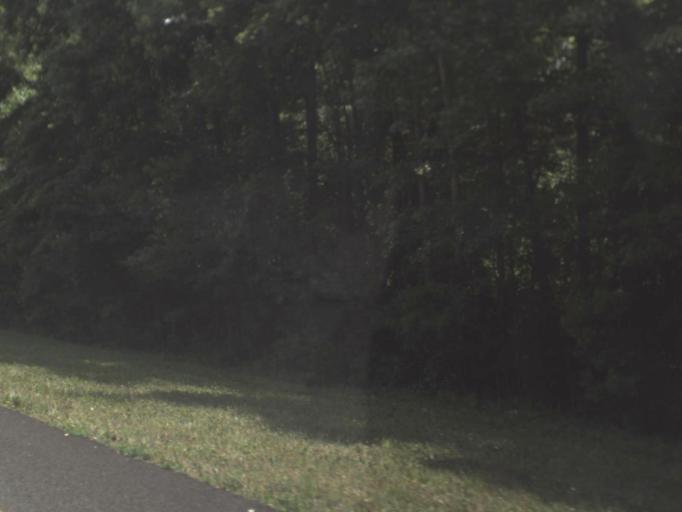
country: US
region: Florida
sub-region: Nassau County
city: Yulee
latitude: 30.6269
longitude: -81.6226
